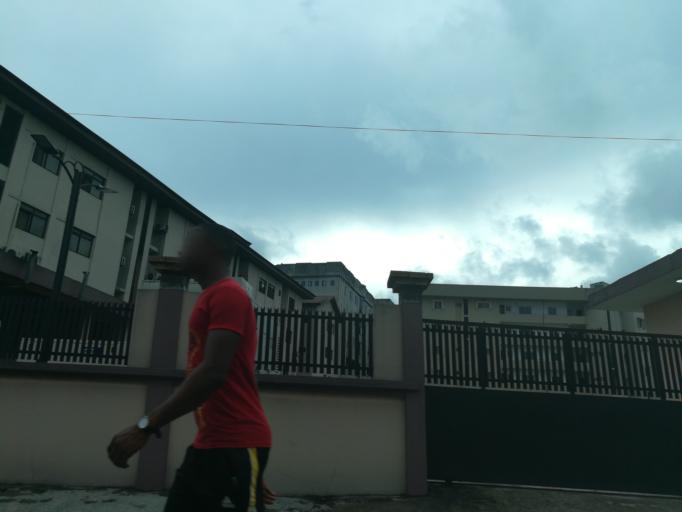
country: NG
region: Rivers
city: Port Harcourt
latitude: 4.8157
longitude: 6.9905
